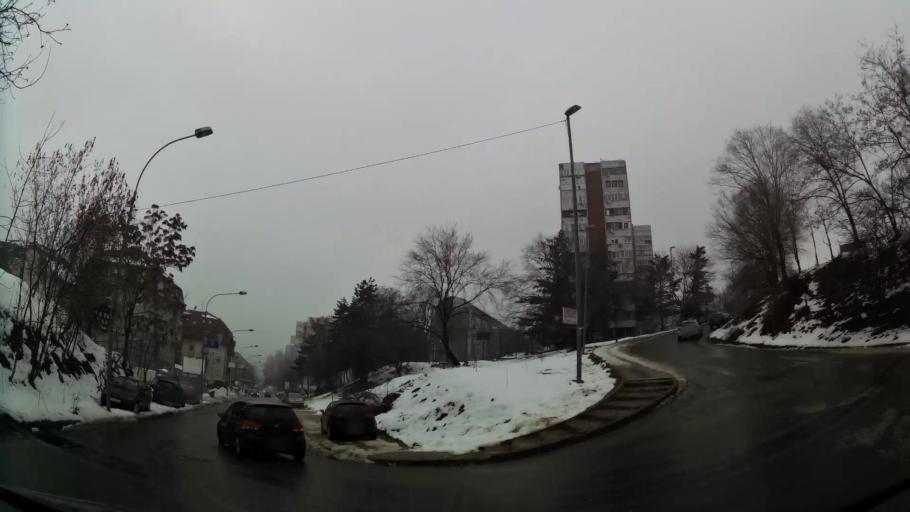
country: RS
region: Central Serbia
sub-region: Belgrade
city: Zvezdara
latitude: 44.7812
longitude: 20.5134
